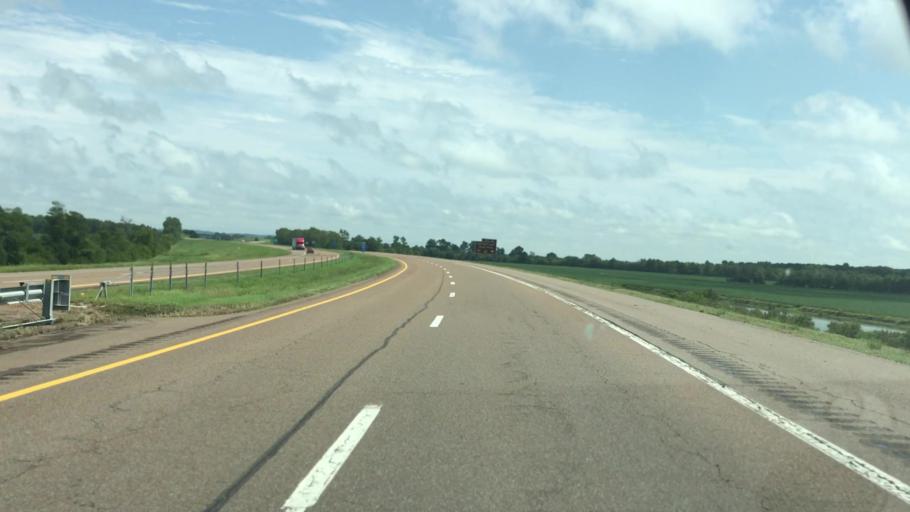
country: US
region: Missouri
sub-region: Pemiscot County
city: Caruthersville
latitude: 36.0967
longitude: -89.6005
